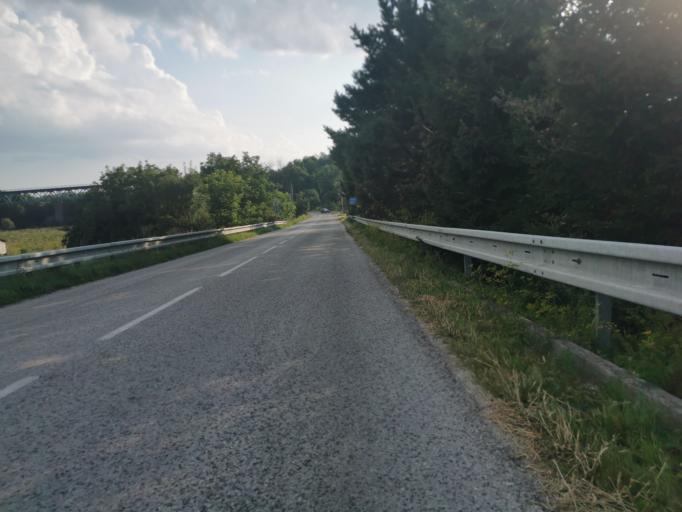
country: SK
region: Trenciansky
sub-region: Okres Myjava
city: Myjava
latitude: 48.7768
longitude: 17.5662
